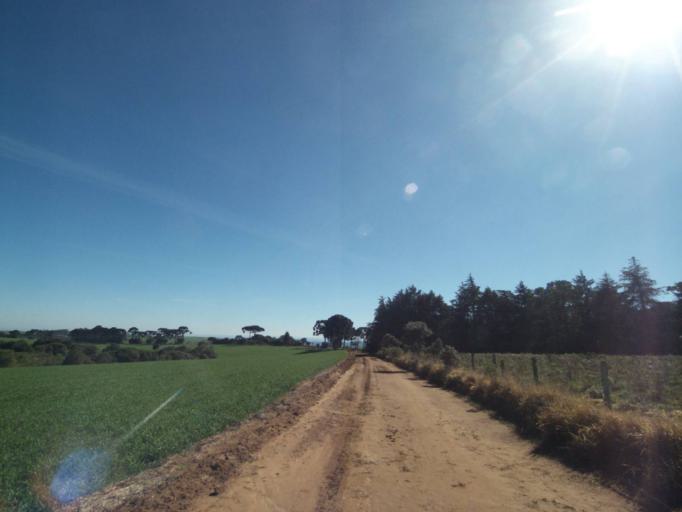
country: BR
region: Parana
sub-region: Tibagi
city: Tibagi
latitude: -24.5967
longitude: -50.2442
